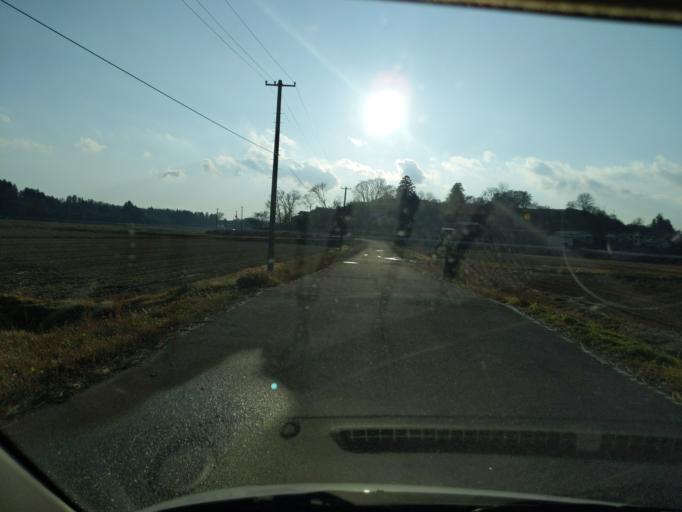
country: JP
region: Miyagi
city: Wakuya
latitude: 38.7096
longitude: 141.1291
